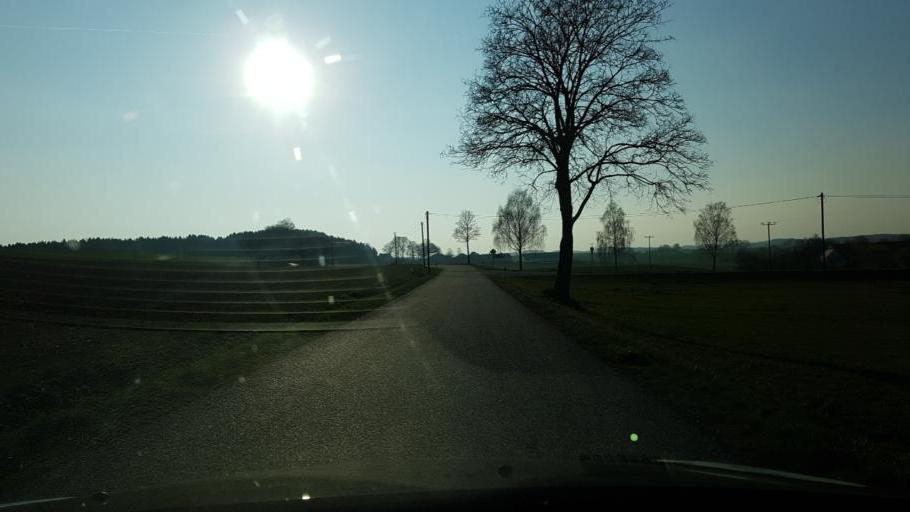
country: DE
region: Bavaria
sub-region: Upper Bavaria
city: Altomunster
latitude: 48.4154
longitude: 11.2459
